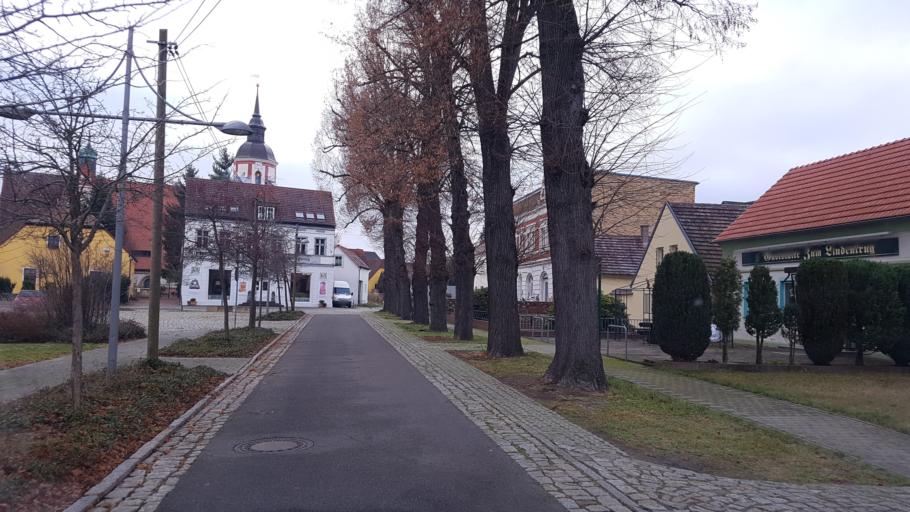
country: DE
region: Brandenburg
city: Schipkau
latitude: 51.5430
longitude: 13.8944
